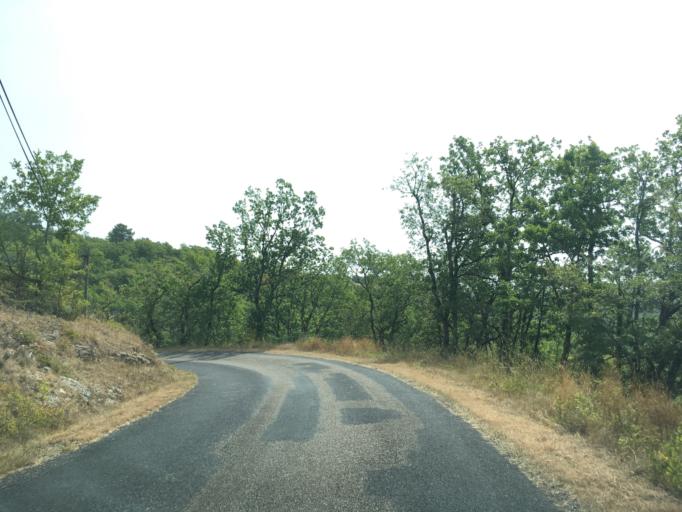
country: FR
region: Midi-Pyrenees
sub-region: Departement du Lot
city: Le Vigan
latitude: 44.7478
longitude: 1.5045
